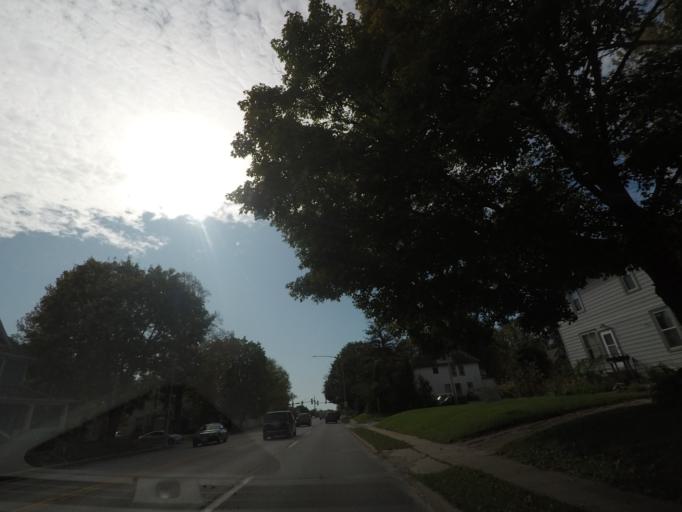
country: US
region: Iowa
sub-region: Story County
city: Ames
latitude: 42.0283
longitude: -93.6204
